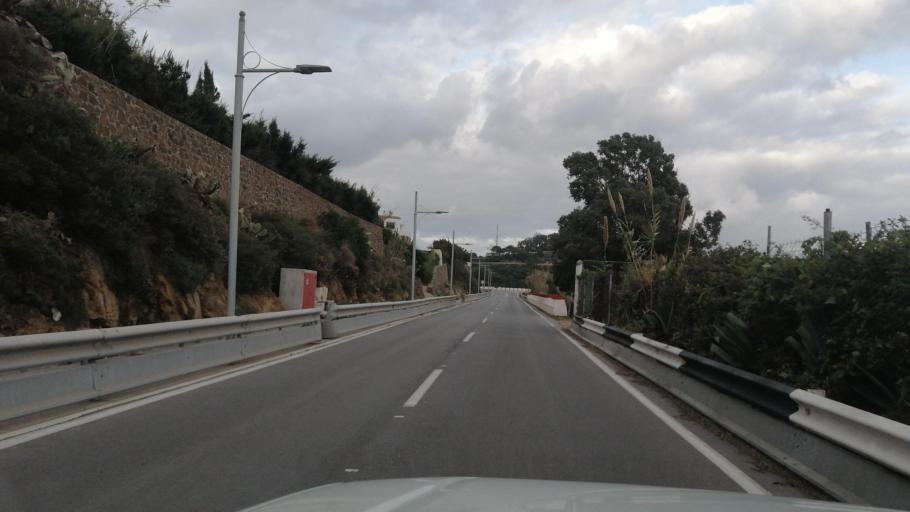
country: ES
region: Ceuta
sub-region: Ceuta
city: Ceuta
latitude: 35.8934
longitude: -5.2865
